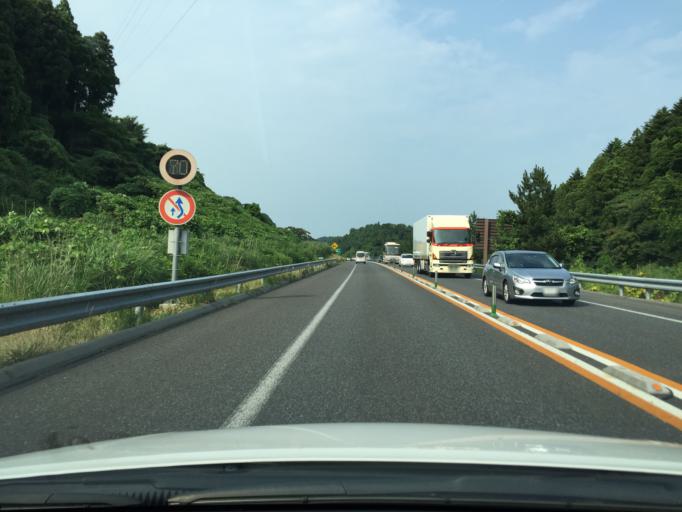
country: JP
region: Fukushima
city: Iwaki
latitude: 37.1352
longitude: 140.9562
